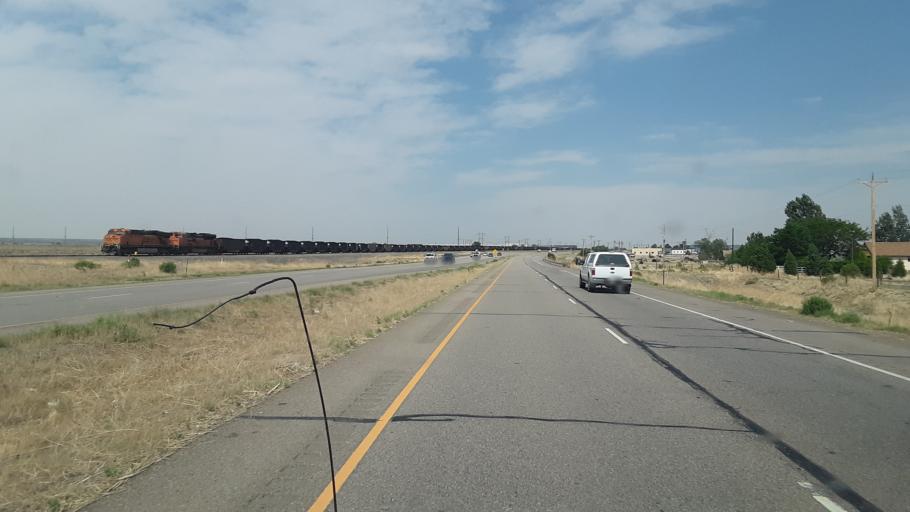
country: US
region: Colorado
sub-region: Pueblo County
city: Pueblo
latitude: 38.2734
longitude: -104.5413
